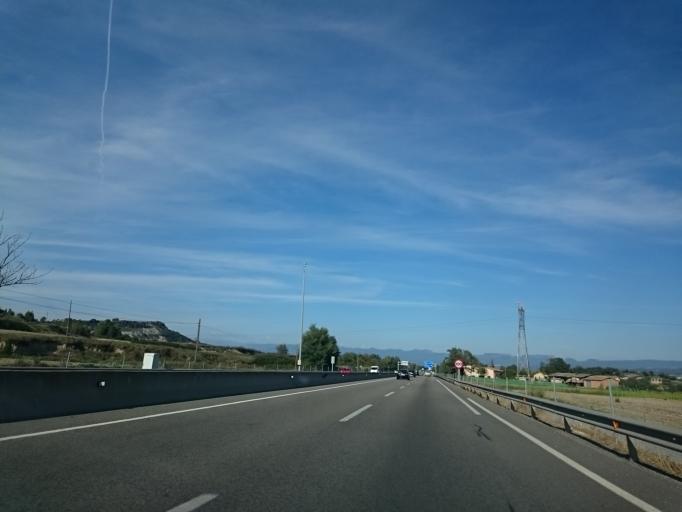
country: ES
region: Catalonia
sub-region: Provincia de Barcelona
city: Tona
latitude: 41.8723
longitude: 2.2351
